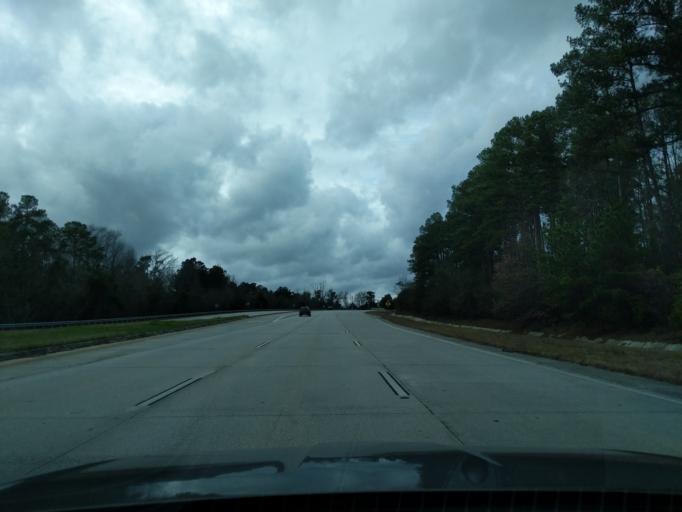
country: US
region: Georgia
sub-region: Columbia County
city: Evans
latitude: 33.4696
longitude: -82.1242
